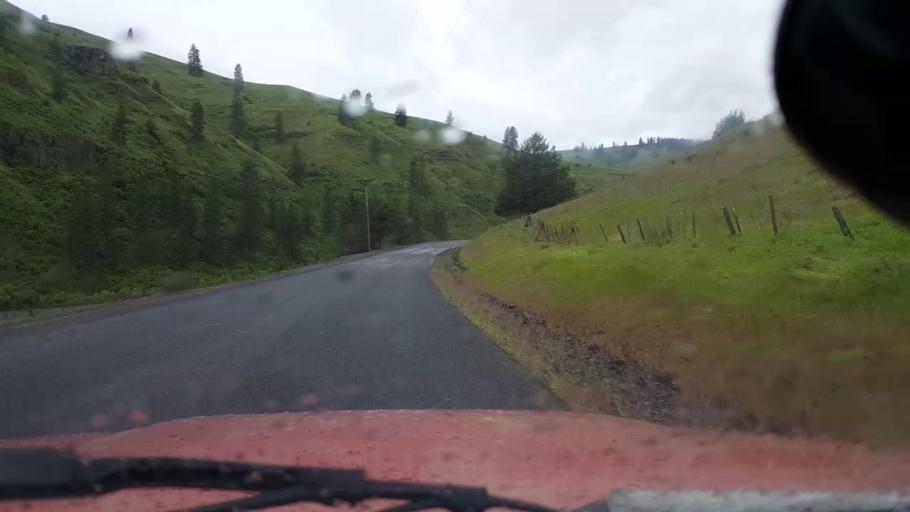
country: US
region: Washington
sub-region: Asotin County
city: Asotin
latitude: 46.0182
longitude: -117.3448
